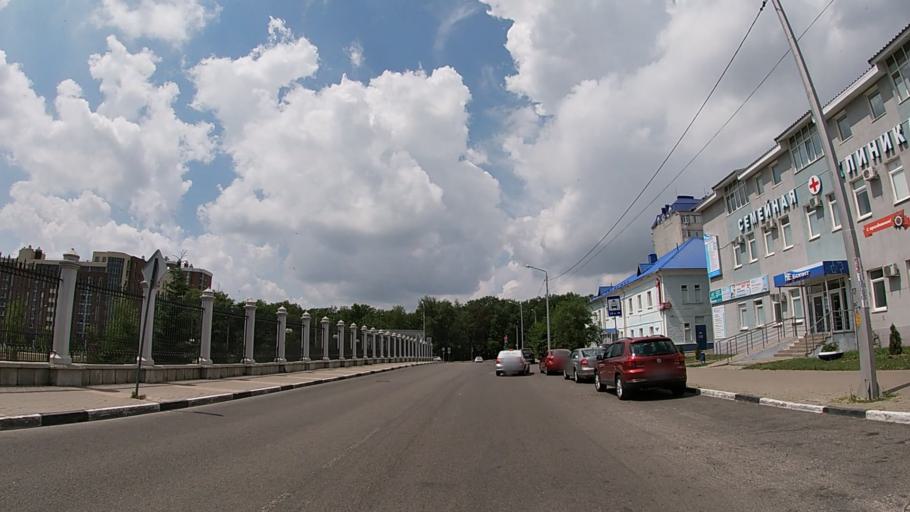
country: RU
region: Belgorod
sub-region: Belgorodskiy Rayon
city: Belgorod
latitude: 50.6068
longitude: 36.5929
